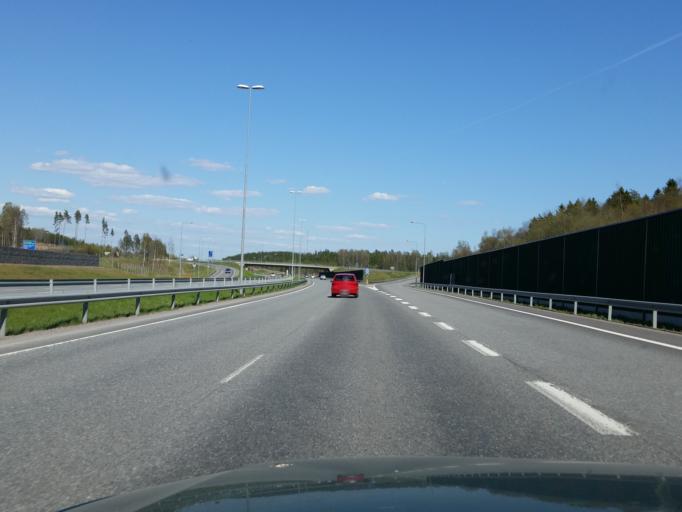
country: FI
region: Uusimaa
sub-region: Helsinki
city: Kirkkonummi
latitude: 60.1172
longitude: 24.4729
